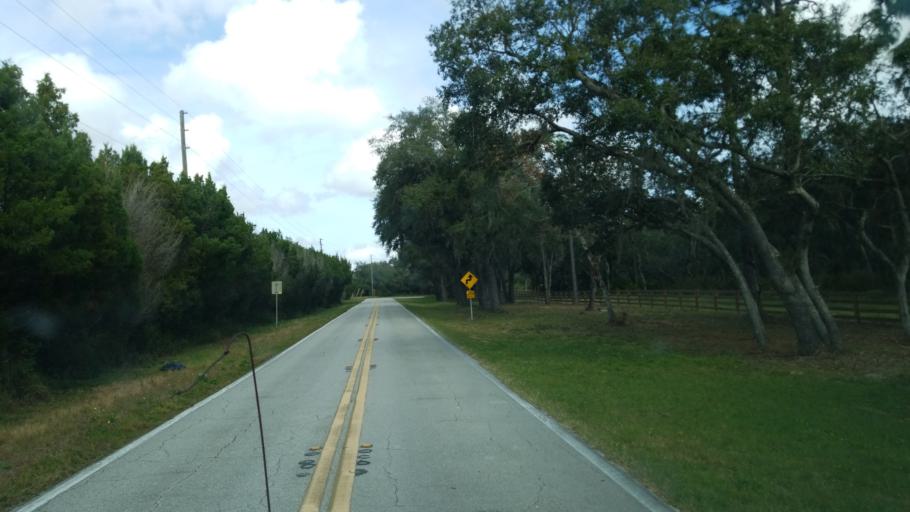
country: US
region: Florida
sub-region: Osceola County
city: Poinciana
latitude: 28.0236
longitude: -81.4960
